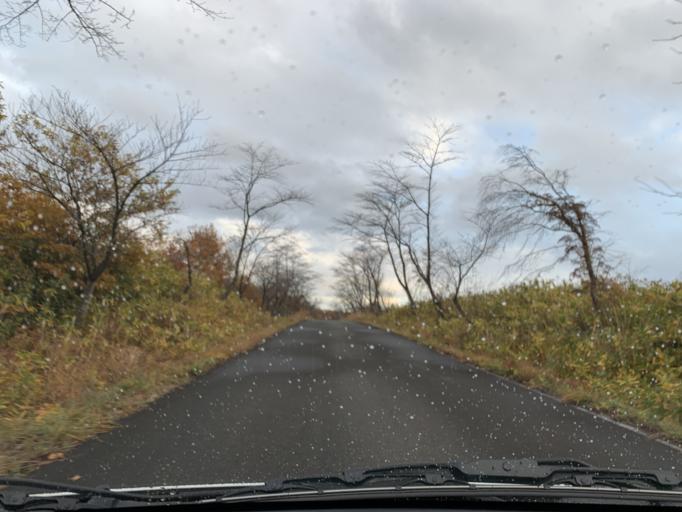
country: JP
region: Iwate
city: Mizusawa
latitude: 39.0881
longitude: 141.0087
